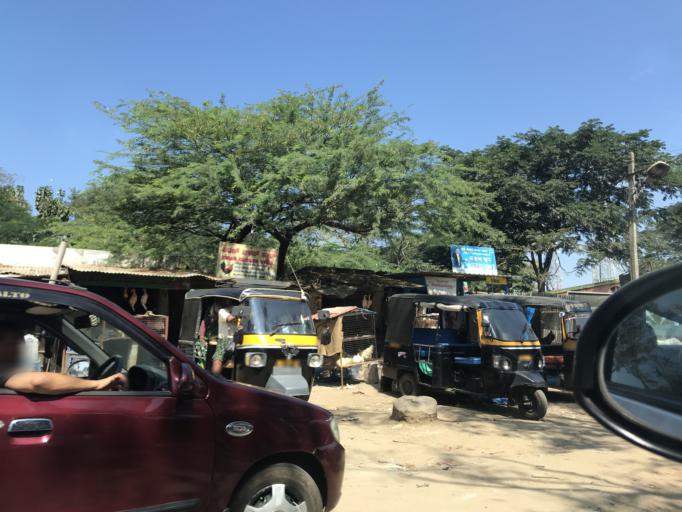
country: IN
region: Karnataka
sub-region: Mysore
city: Heggadadevankote
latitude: 12.0661
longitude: 76.3551
